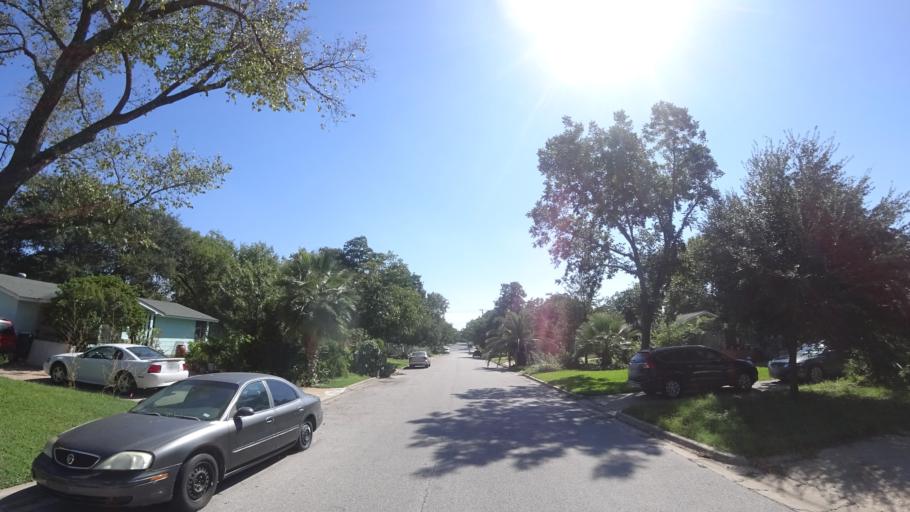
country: US
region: Texas
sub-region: Travis County
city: Austin
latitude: 30.3083
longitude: -97.6977
